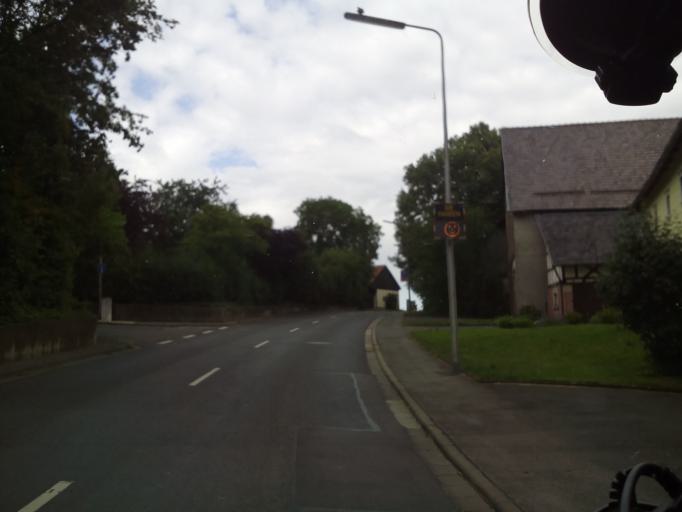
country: DE
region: Bavaria
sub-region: Upper Franconia
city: Rodental
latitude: 50.2541
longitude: 11.0823
